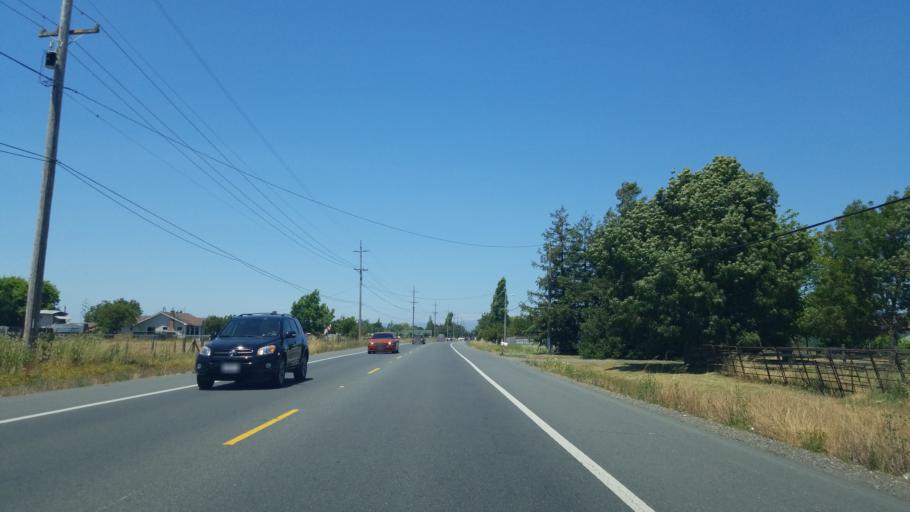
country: US
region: California
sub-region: Sonoma County
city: Roseland
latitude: 38.3805
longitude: -122.7415
